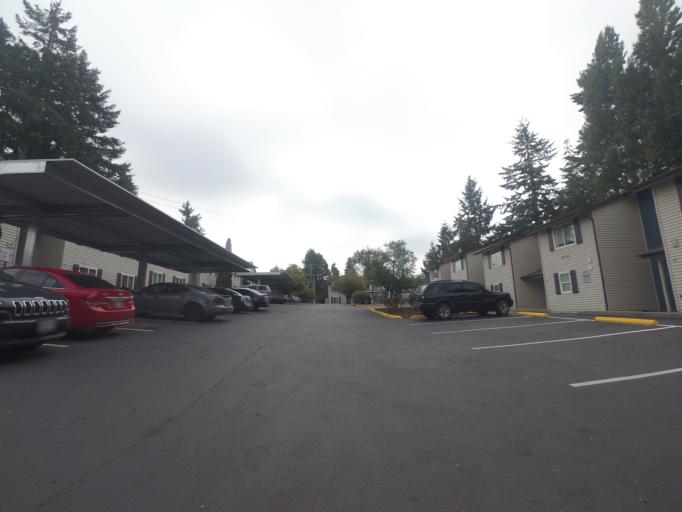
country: US
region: Washington
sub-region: Pierce County
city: Fircrest
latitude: 47.2056
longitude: -122.5080
